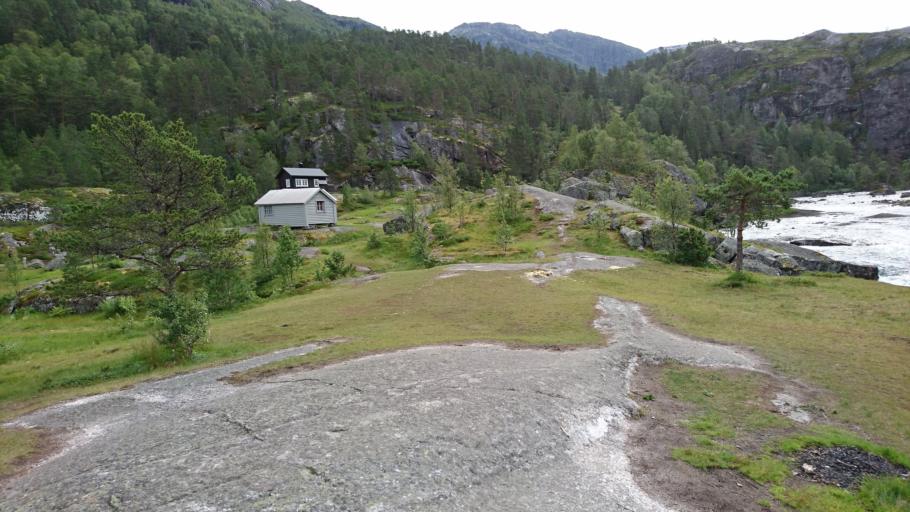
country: NO
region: Hordaland
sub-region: Ullensvang
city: Kinsarvik
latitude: 60.3463
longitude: 6.7881
